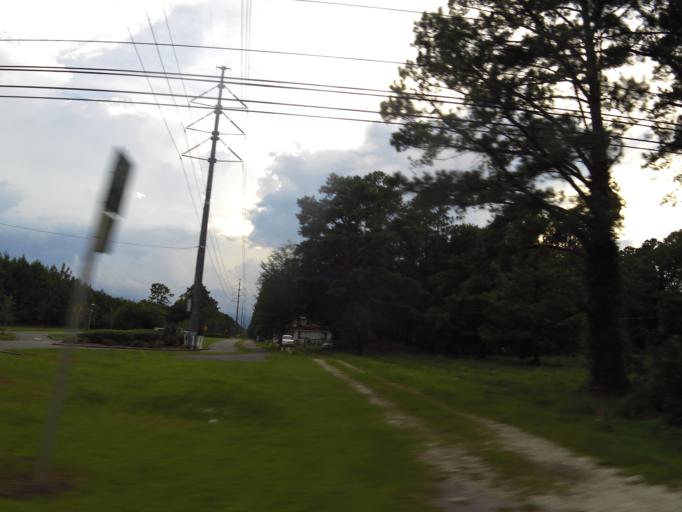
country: US
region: Florida
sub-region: Duval County
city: Jacksonville
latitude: 30.3456
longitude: -81.7728
